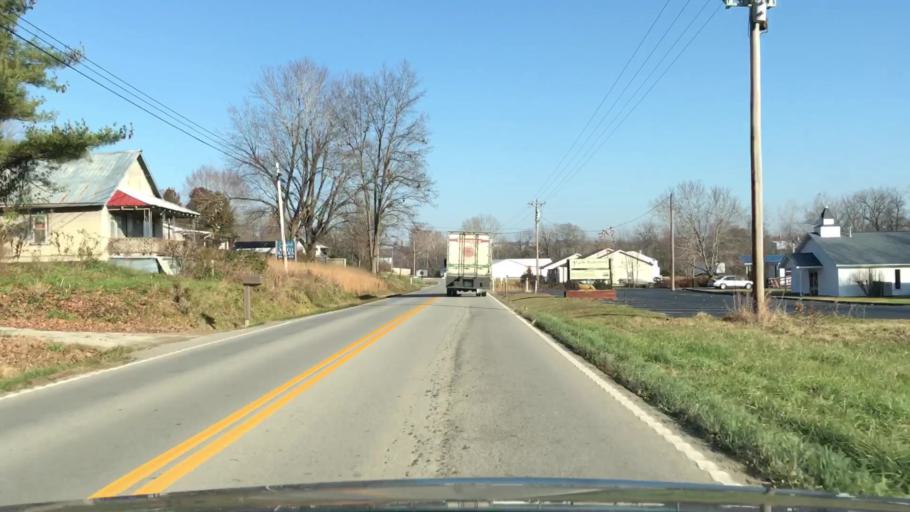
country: US
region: Kentucky
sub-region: Grayson County
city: Leitchfield
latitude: 37.4582
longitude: -86.2904
